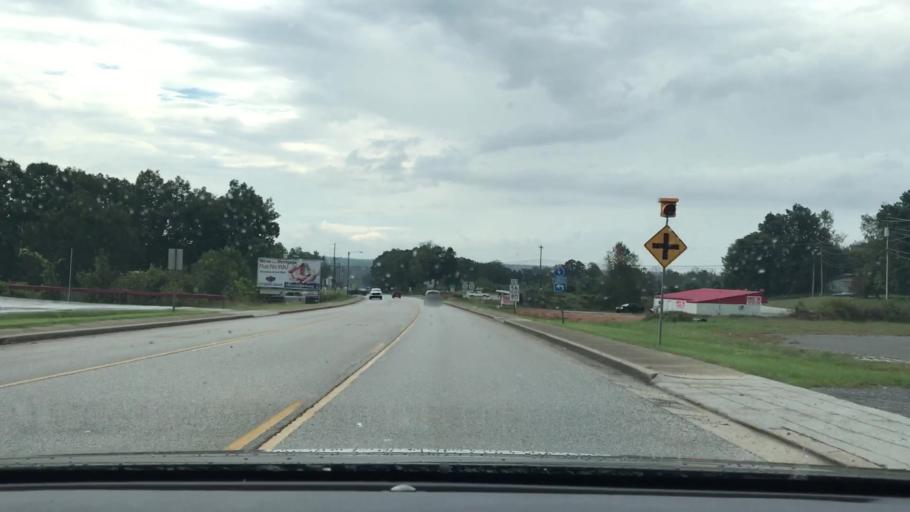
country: US
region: Tennessee
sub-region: Macon County
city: Red Boiling Springs
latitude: 36.5199
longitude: -85.8612
